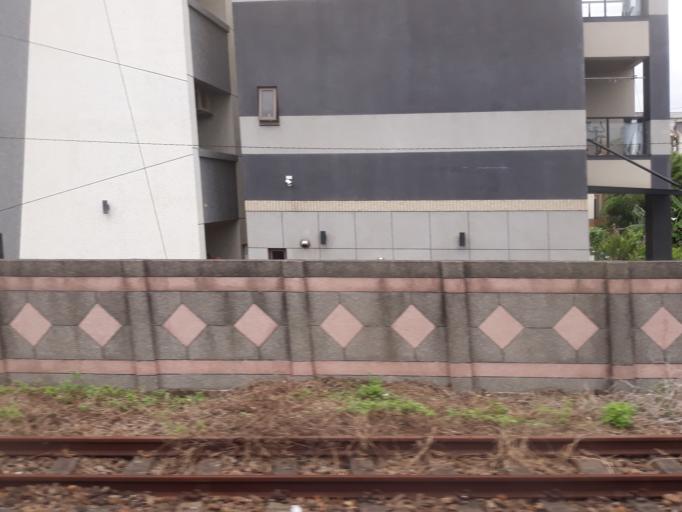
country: TW
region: Taiwan
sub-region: Yilan
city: Yilan
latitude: 24.7012
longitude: 121.7753
